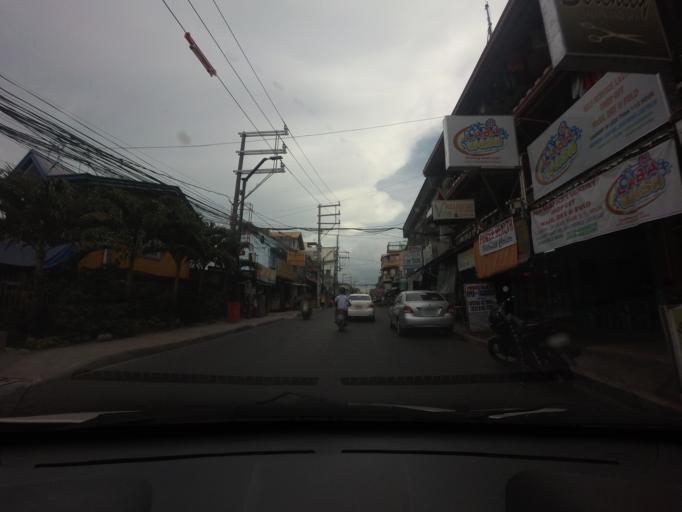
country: PH
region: Calabarzon
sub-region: Province of Rizal
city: Taguig
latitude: 14.5082
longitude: 121.0536
